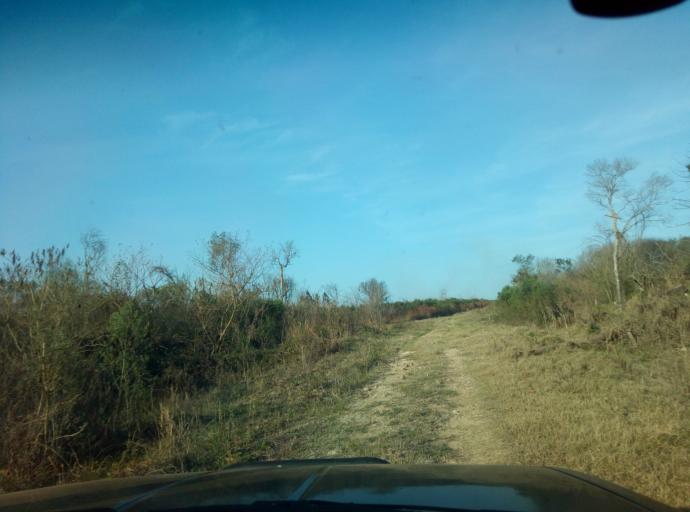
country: PY
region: Caaguazu
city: Doctor Cecilio Baez
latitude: -25.2000
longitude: -56.1256
